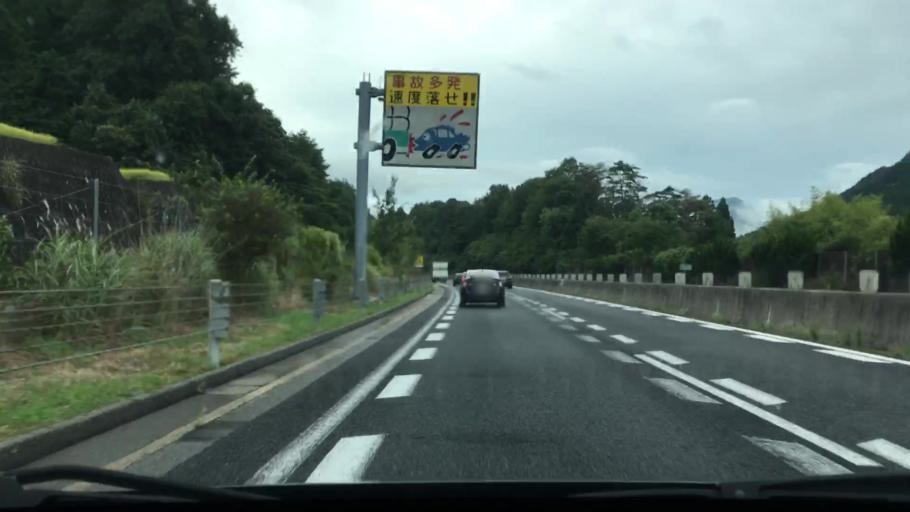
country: JP
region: Hiroshima
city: Hiroshima-shi
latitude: 34.5974
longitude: 132.4897
